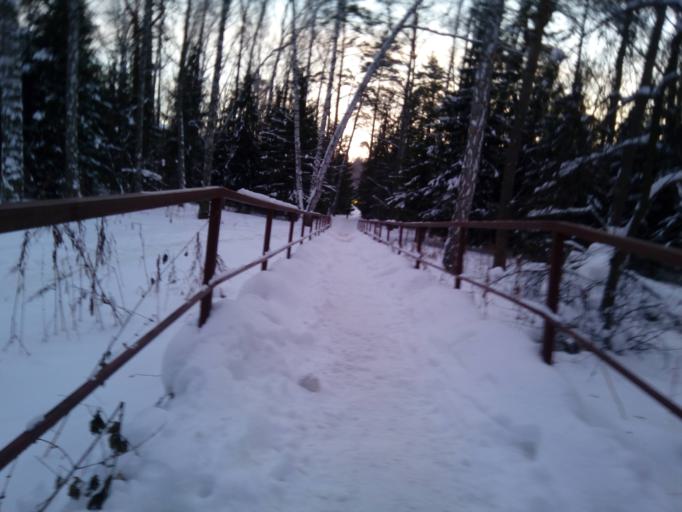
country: RU
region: Novosibirsk
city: Akademgorodok
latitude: 54.8406
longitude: 83.0892
